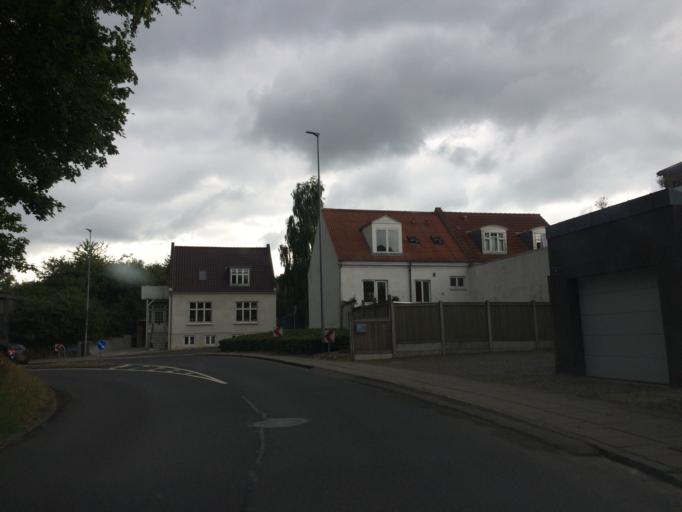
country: DK
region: Central Jutland
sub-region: Silkeborg Kommune
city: Silkeborg
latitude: 56.1643
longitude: 9.5358
